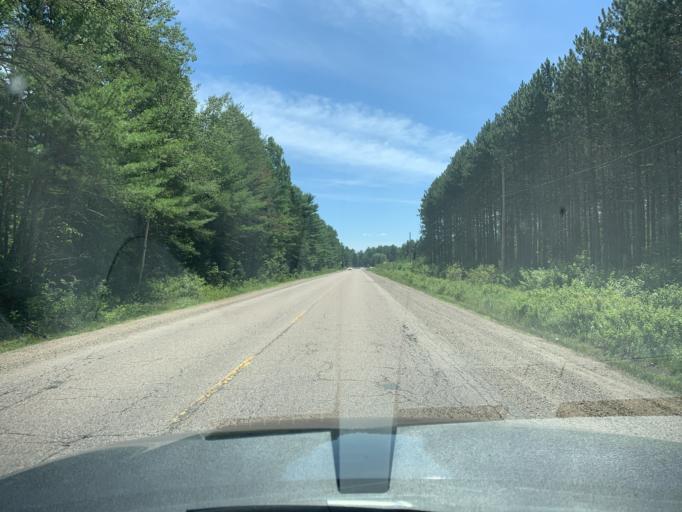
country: CA
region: Ontario
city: Petawawa
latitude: 45.6490
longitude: -77.5776
